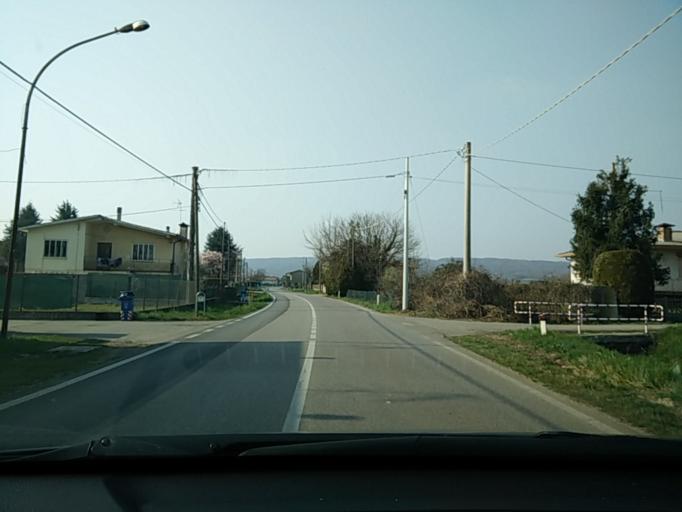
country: IT
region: Veneto
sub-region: Provincia di Treviso
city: Selva del Montello
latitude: 45.7699
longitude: 12.1478
